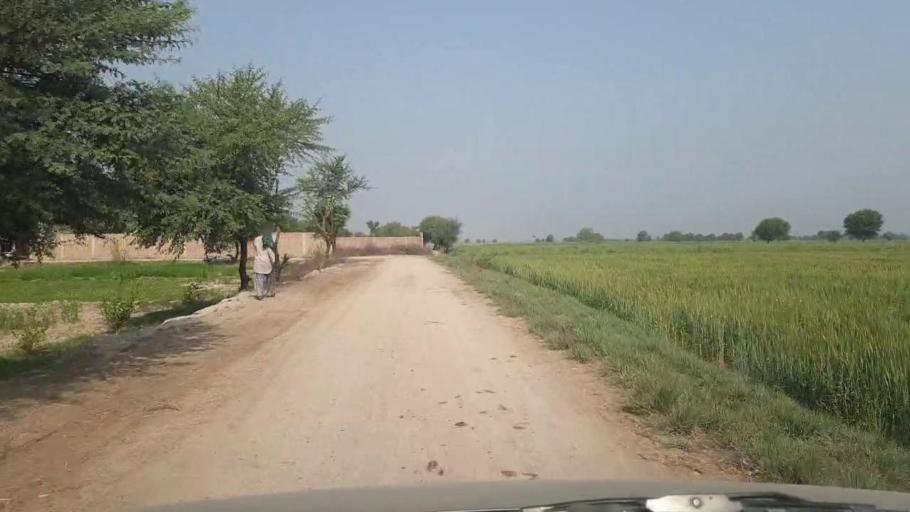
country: PK
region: Sindh
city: Umarkot
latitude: 25.4074
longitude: 69.7184
